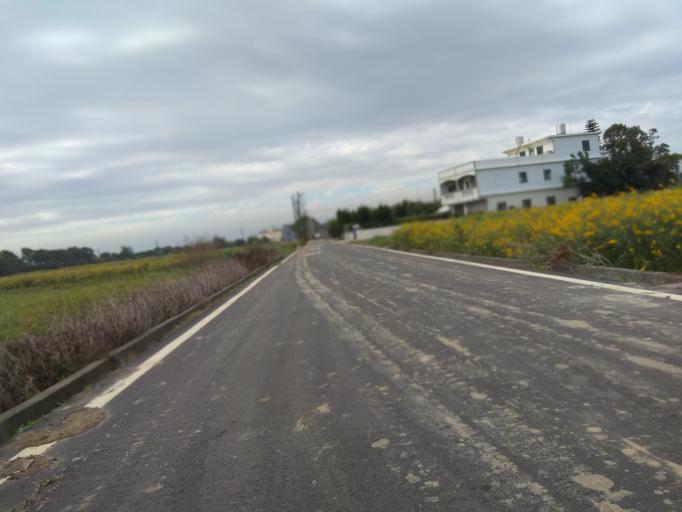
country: TW
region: Taiwan
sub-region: Hsinchu
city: Zhubei
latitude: 24.9843
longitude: 121.0489
